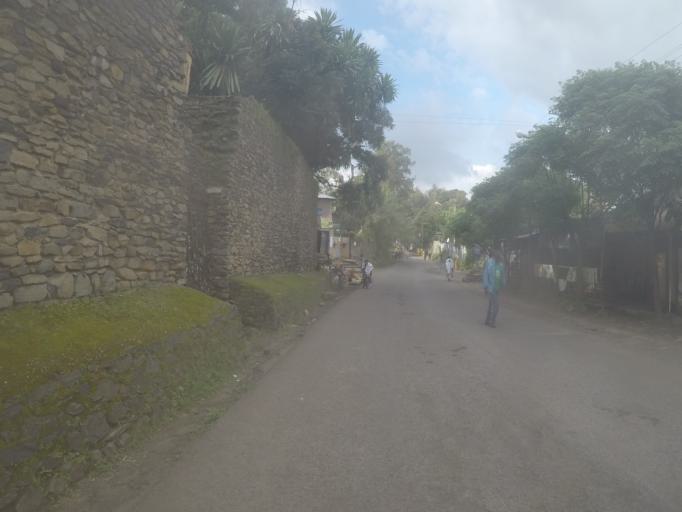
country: ET
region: Amhara
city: Gondar
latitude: 12.6087
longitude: 37.4708
